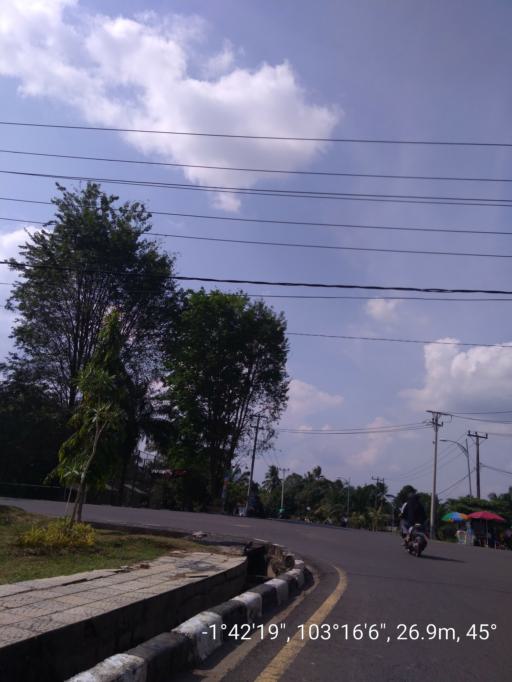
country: ID
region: Jambi
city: Muara Bulian
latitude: -1.7053
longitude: 103.2684
